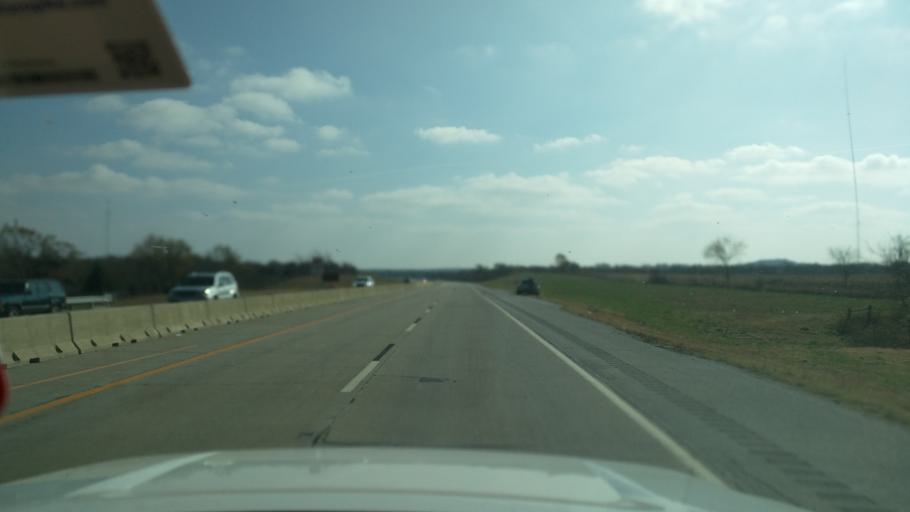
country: US
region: Oklahoma
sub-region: Wagoner County
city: Coweta
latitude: 35.9880
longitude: -95.6229
